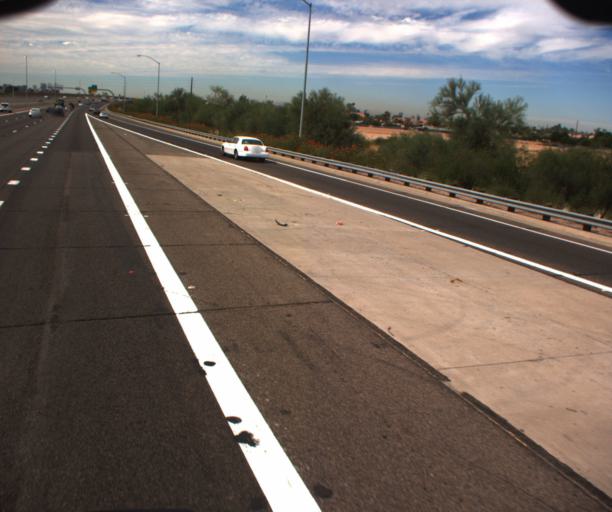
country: US
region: Arizona
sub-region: Maricopa County
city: Tempe Junction
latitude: 33.4594
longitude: -112.0001
